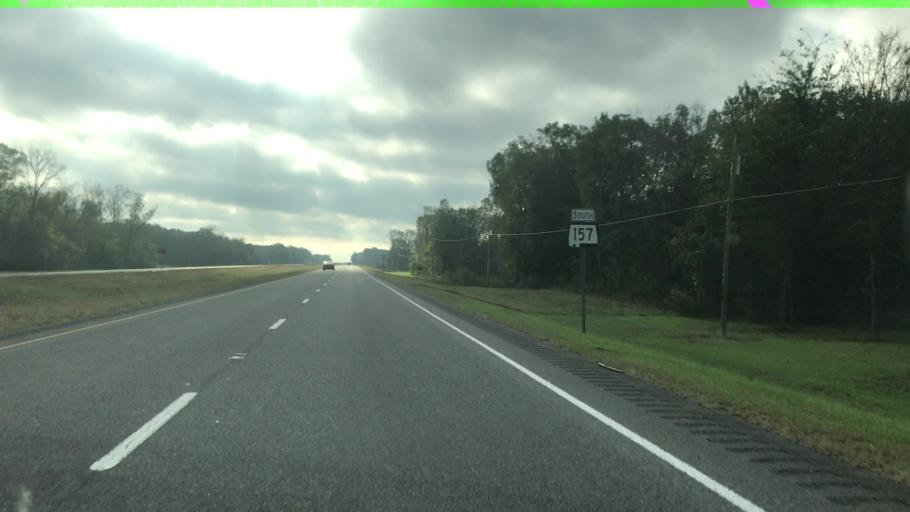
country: US
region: Alabama
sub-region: Morgan County
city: Danville
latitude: 34.4095
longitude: -87.1486
